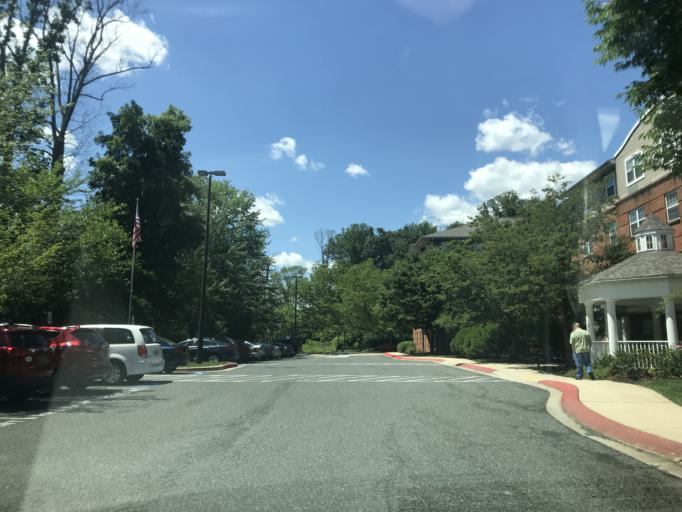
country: US
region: Maryland
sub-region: Harford County
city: Bel Air
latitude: 39.5272
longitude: -76.3477
